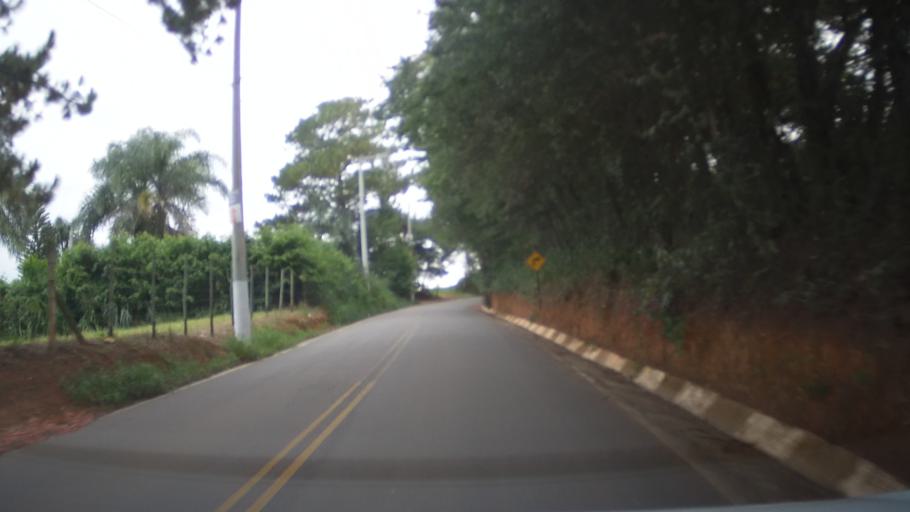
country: BR
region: Sao Paulo
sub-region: Vinhedo
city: Vinhedo
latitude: -23.0790
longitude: -47.0279
